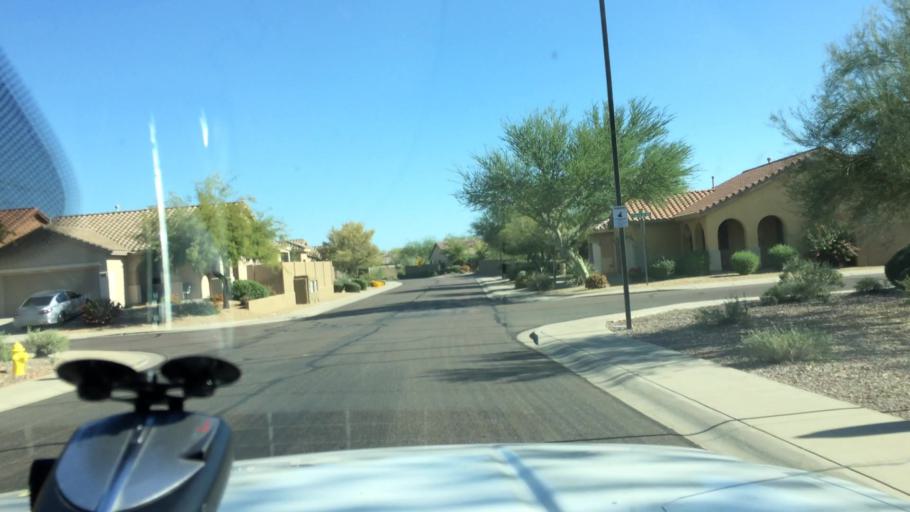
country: US
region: Arizona
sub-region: Maricopa County
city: Anthem
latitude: 33.8563
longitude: -112.1138
